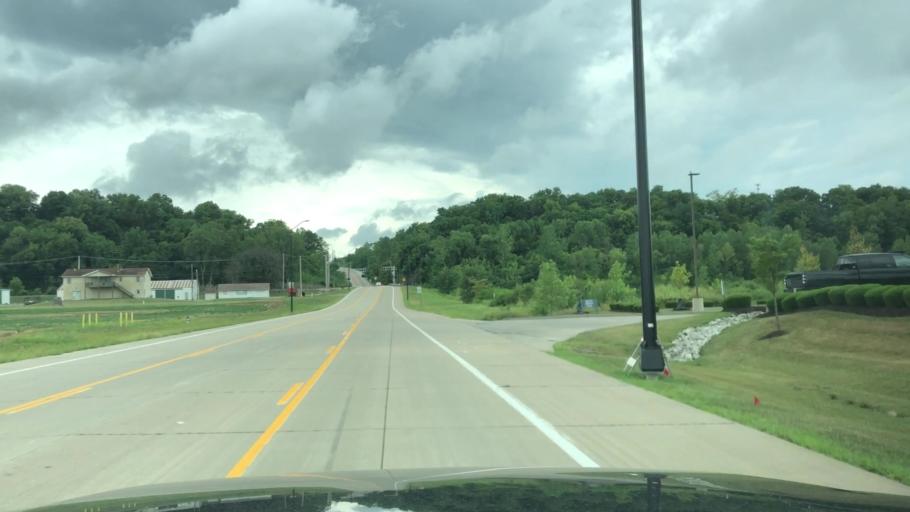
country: US
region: Missouri
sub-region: Saint Charles County
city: Saint Peters
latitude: 38.8070
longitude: -90.5808
